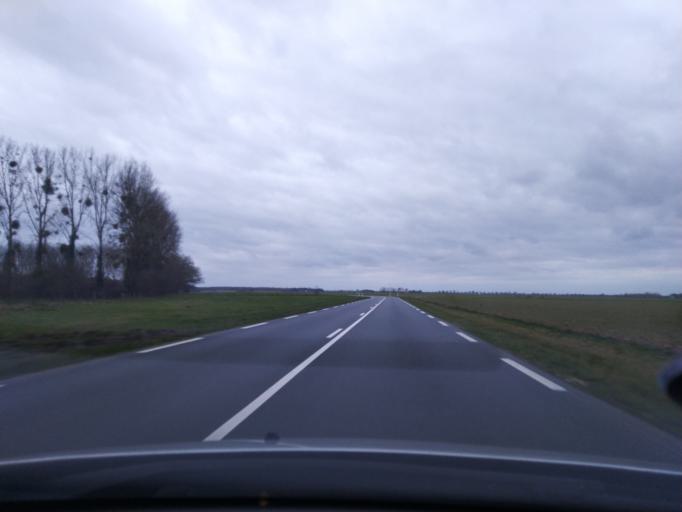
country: FR
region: Picardie
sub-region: Departement de la Somme
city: Crecy-en-Ponthieu
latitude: 50.1913
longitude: 1.8722
